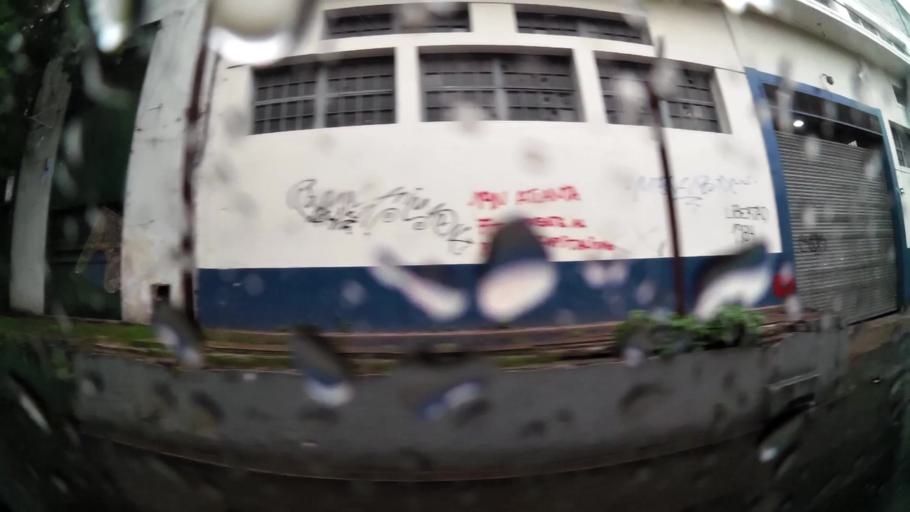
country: AR
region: Buenos Aires
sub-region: Partido de Avellaneda
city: Avellaneda
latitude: -34.6410
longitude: -58.3633
